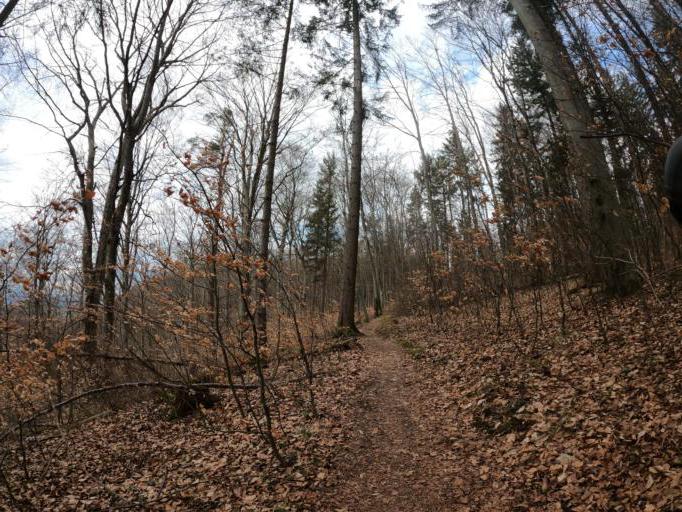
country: DE
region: Baden-Wuerttemberg
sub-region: Tuebingen Region
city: Gomaringen
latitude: 48.3990
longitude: 9.1380
